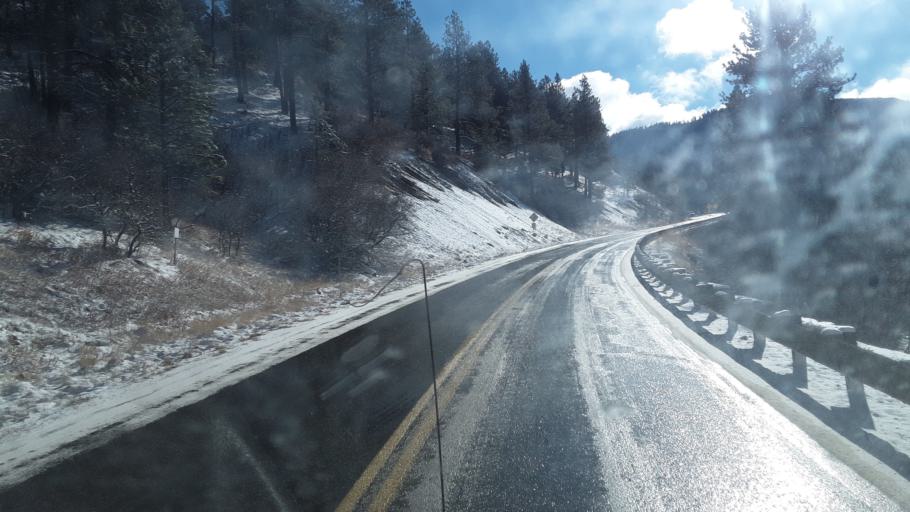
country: US
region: Colorado
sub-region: La Plata County
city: Durango
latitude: 37.3327
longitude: -107.7390
